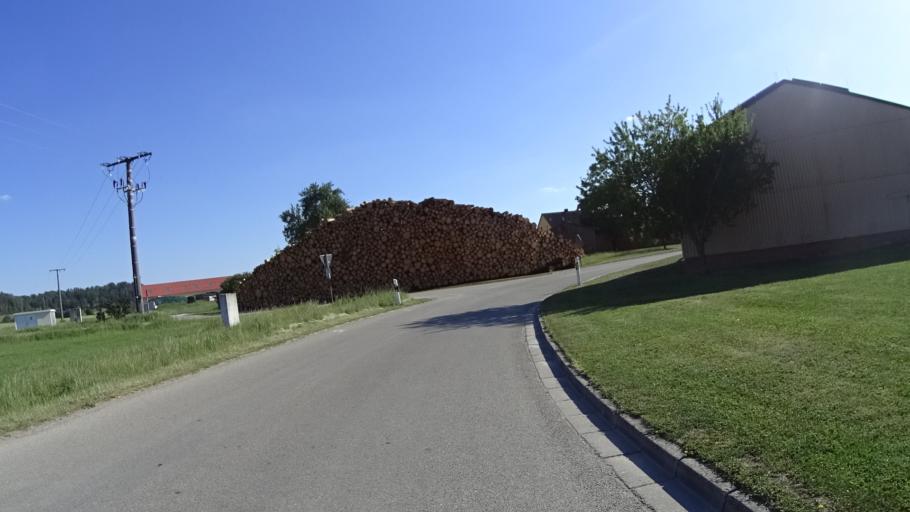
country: DE
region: Bavaria
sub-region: Regierungsbezirk Mittelfranken
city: Feuchtwangen
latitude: 49.1926
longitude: 10.3222
